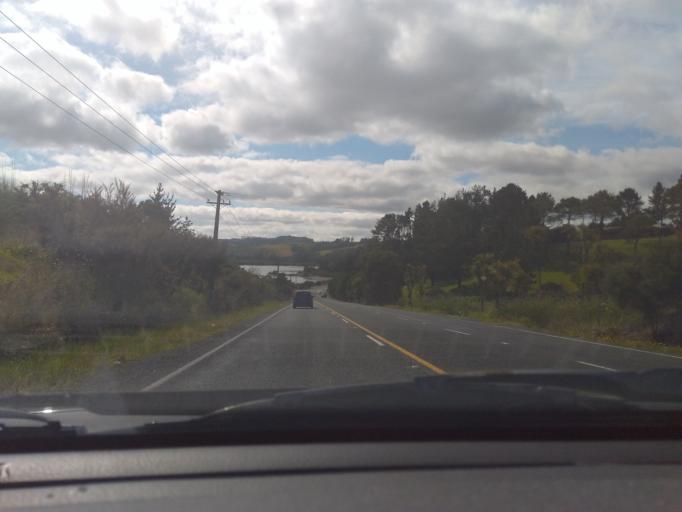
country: NZ
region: Northland
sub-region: Far North District
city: Taipa
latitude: -34.9975
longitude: 173.5323
